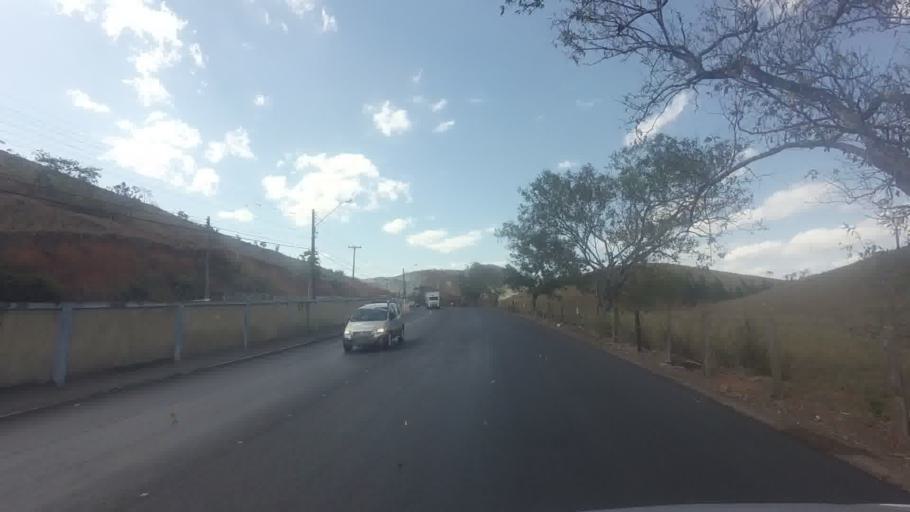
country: BR
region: Rio de Janeiro
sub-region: Bom Jesus Do Itabapoana
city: Bom Jesus do Itabapoana
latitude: -21.1405
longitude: -41.6629
